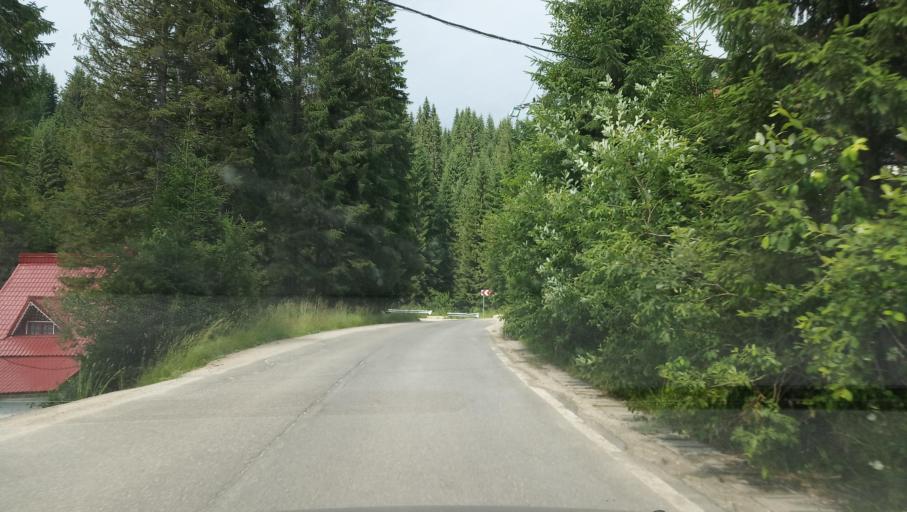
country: RO
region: Dambovita
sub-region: Comuna Moroeni
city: Glod
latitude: 45.3339
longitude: 25.4297
